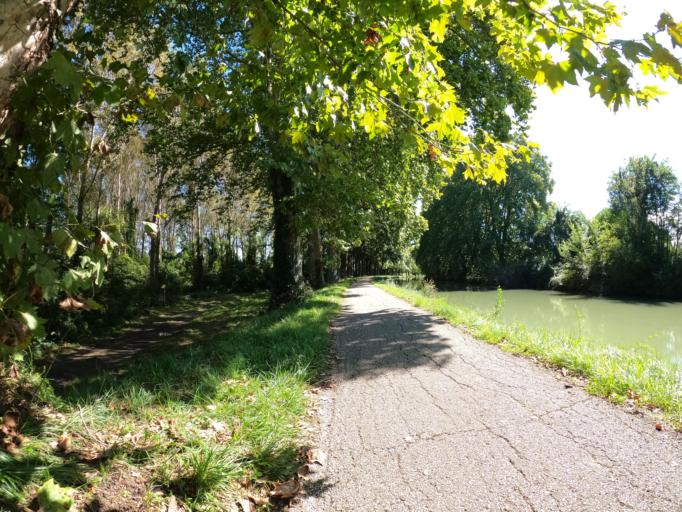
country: FR
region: Midi-Pyrenees
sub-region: Departement du Tarn-et-Garonne
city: Lamagistere
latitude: 44.1398
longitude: 0.8124
